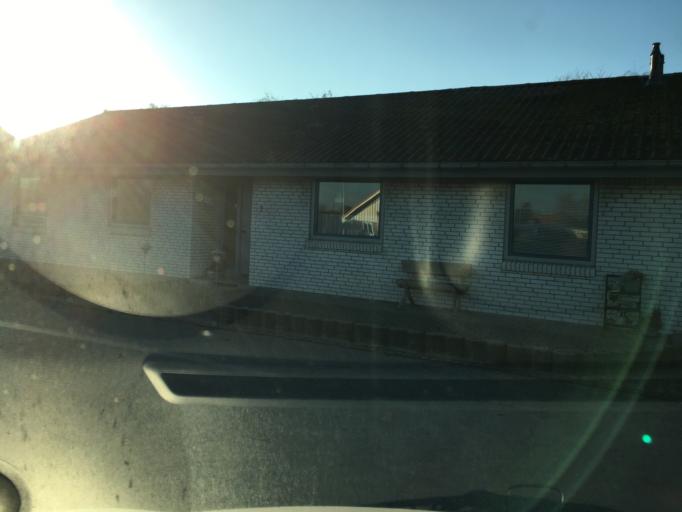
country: DK
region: South Denmark
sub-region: Tonder Kommune
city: Tonder
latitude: 54.9365
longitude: 8.8471
